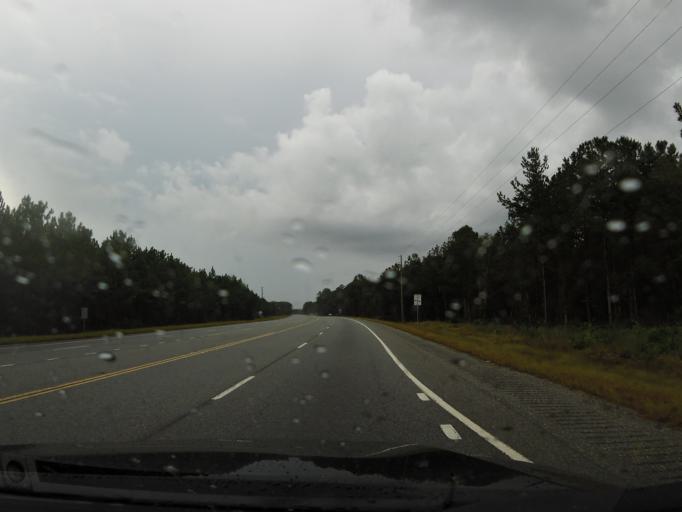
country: US
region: Georgia
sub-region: Wayne County
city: Jesup
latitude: 31.5529
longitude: -81.8156
